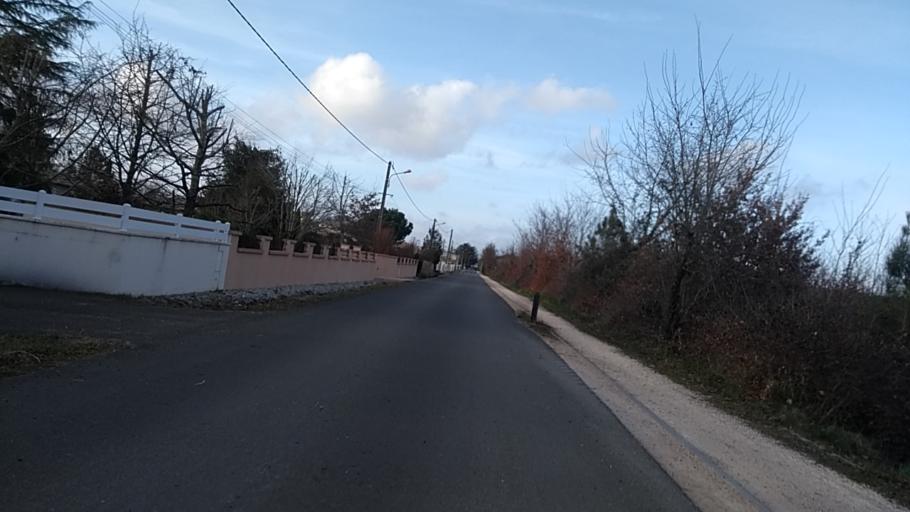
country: FR
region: Aquitaine
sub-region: Departement de la Gironde
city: Le Barp
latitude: 44.5980
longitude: -0.7682
